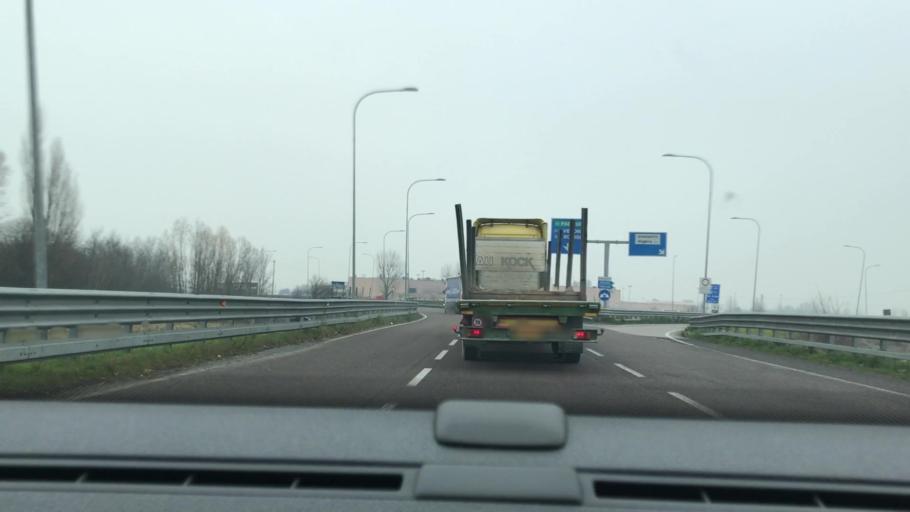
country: IT
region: Veneto
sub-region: Provincia di Rovigo
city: Bosaro
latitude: 45.0254
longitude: 11.7751
